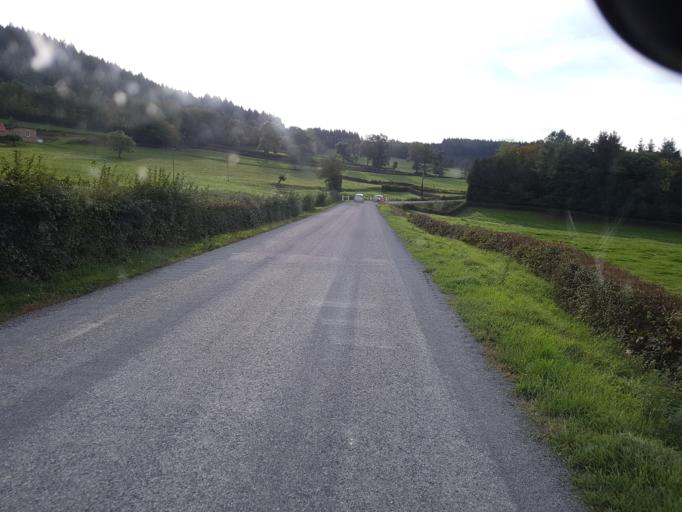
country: FR
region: Bourgogne
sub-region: Departement de Saone-et-Loire
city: Chauffailles
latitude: 46.2600
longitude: 4.4015
